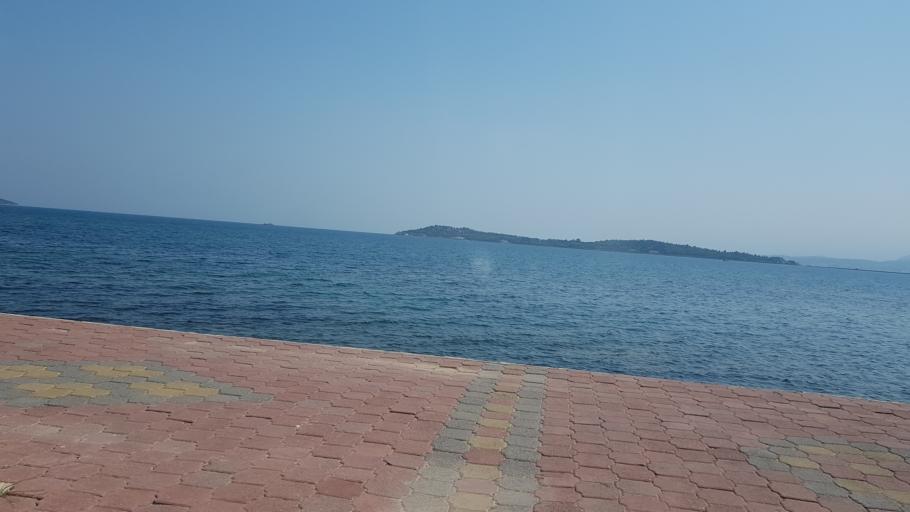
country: TR
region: Izmir
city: Urla
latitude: 38.3692
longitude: 26.7642
